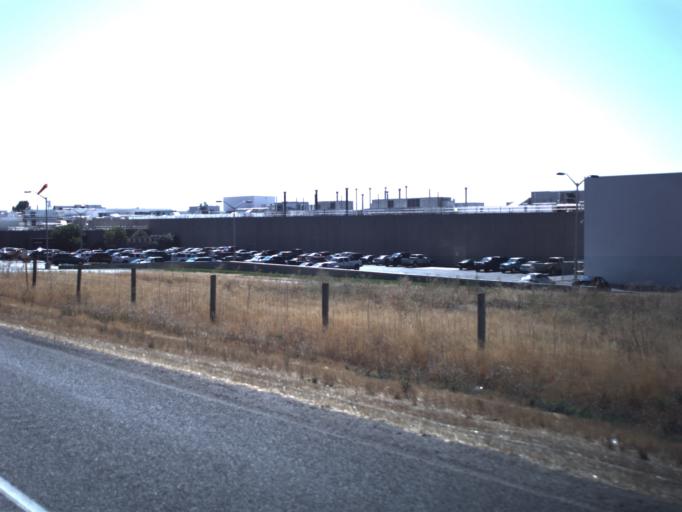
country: US
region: Utah
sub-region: Cache County
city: Richmond
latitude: 41.9418
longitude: -111.8139
